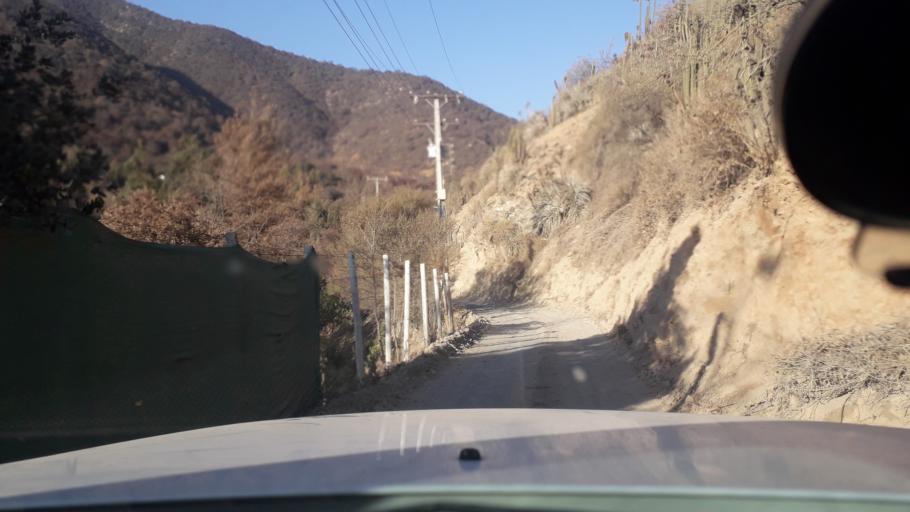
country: CL
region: Valparaiso
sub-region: Provincia de Marga Marga
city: Limache
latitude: -33.0516
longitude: -71.0856
